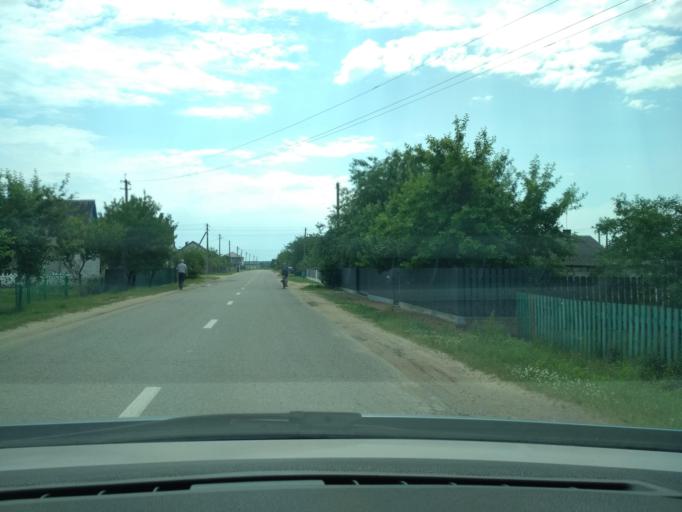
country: BY
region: Grodnenskaya
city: Astravyets
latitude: 54.6059
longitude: 25.9593
